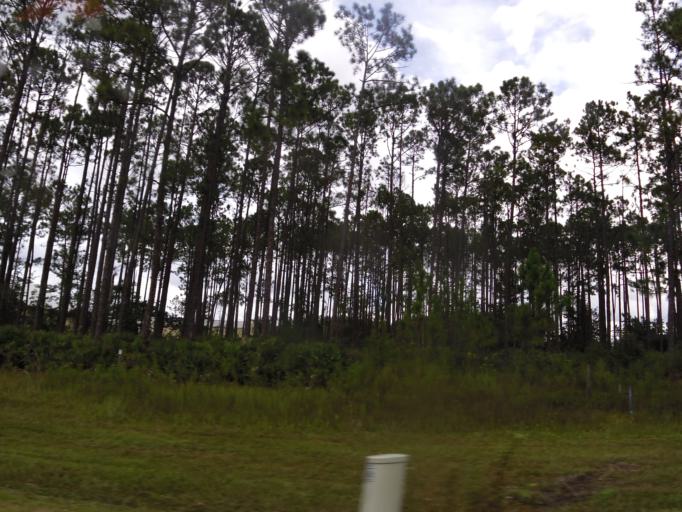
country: US
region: Florida
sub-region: Clay County
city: Middleburg
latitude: 30.0629
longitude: -81.9000
